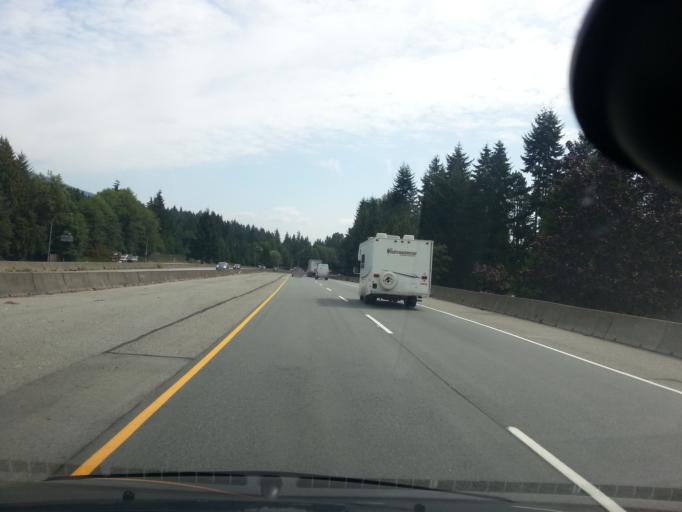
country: CA
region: British Columbia
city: West Vancouver
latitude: 49.3376
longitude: -123.1343
